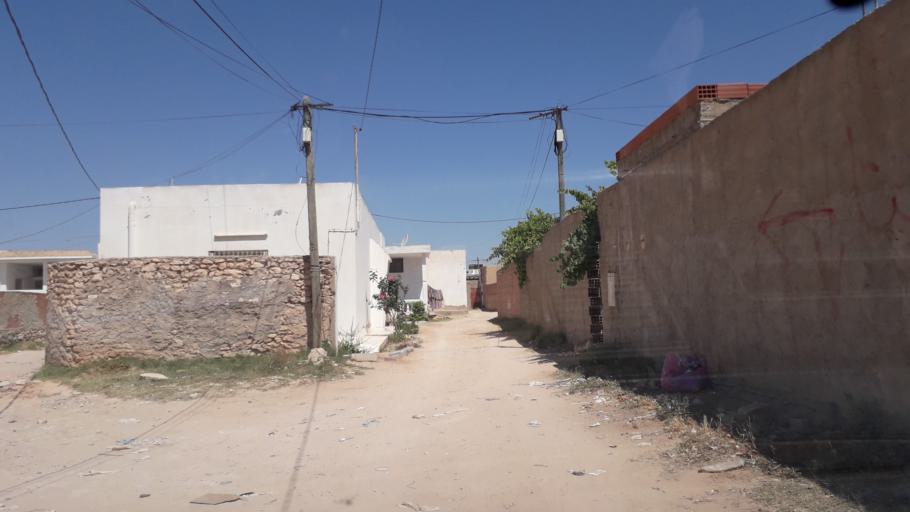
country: TN
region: Safaqis
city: Al Qarmadah
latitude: 34.8232
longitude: 10.7665
